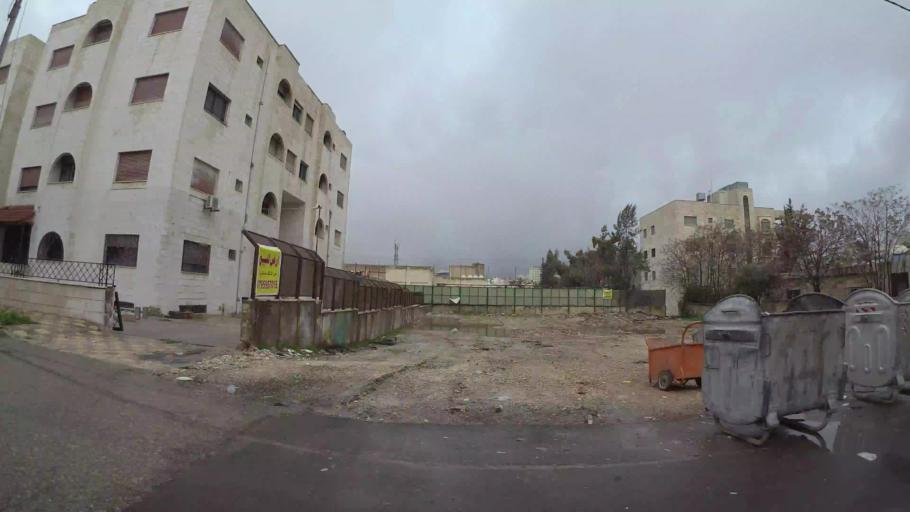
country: JO
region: Amman
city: Wadi as Sir
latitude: 31.9637
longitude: 35.8617
